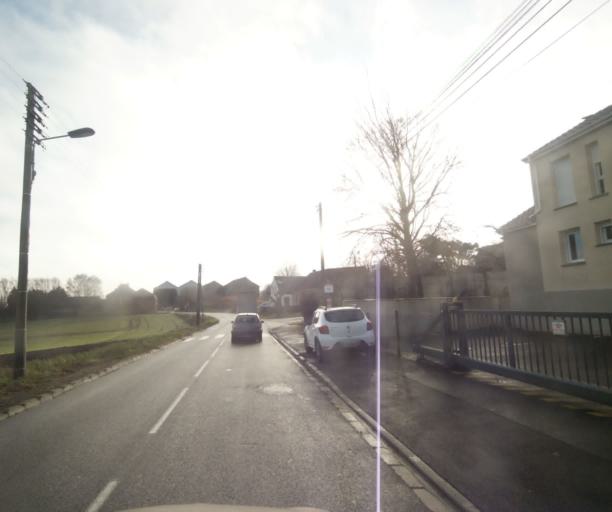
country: FR
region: Nord-Pas-de-Calais
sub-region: Departement du Nord
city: Artres
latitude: 50.2866
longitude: 3.5461
